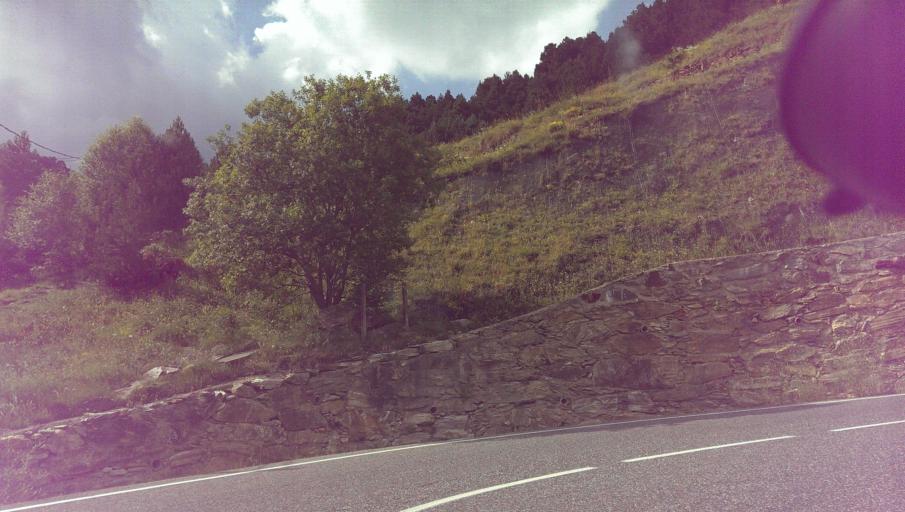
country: AD
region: Canillo
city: Canillo
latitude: 42.5709
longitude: 1.5941
